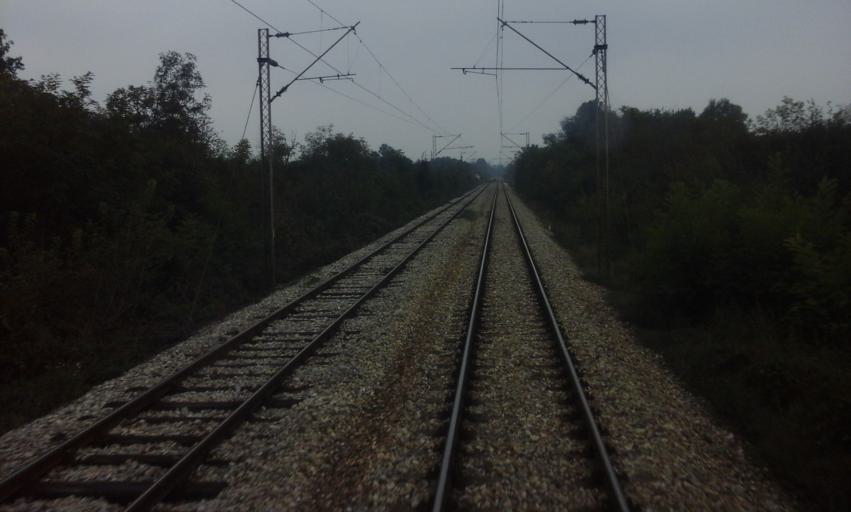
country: RS
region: Central Serbia
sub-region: Podunavski Okrug
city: Velika Plana
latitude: 44.2652
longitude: 21.0914
